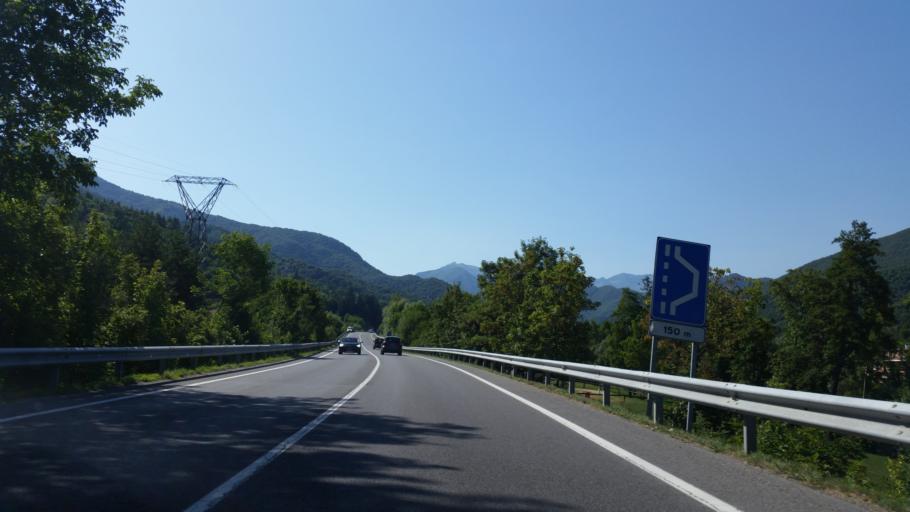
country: IT
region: Piedmont
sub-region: Provincia di Cuneo
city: Robilante
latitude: 44.2949
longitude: 7.5164
